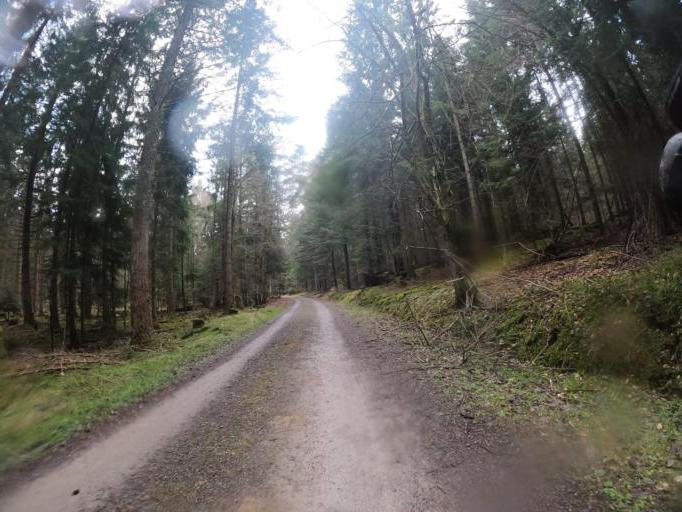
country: DE
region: Baden-Wuerttemberg
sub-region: Karlsruhe Region
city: Schomberg
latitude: 48.7620
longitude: 8.6392
